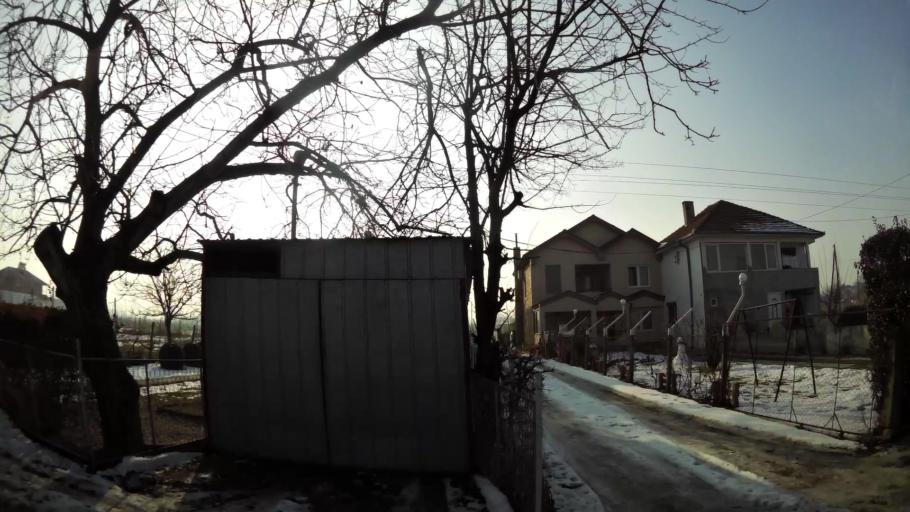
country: MK
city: Kadino
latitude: 41.9633
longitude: 21.5984
